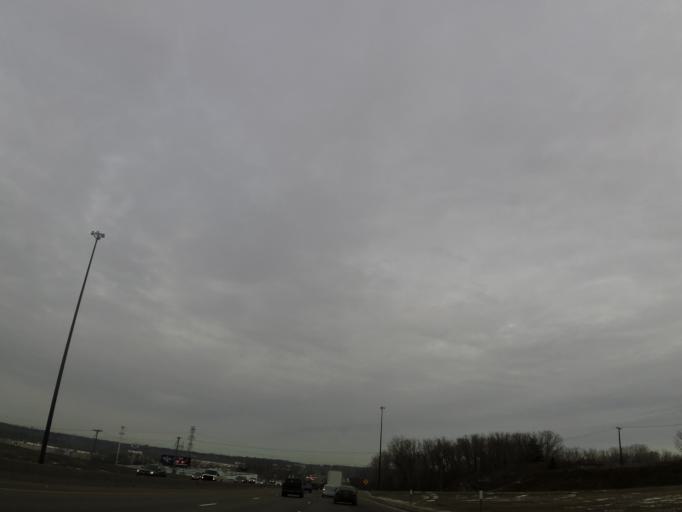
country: US
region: Minnesota
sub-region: Dakota County
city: Burnsville
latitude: 44.7760
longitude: -93.2881
